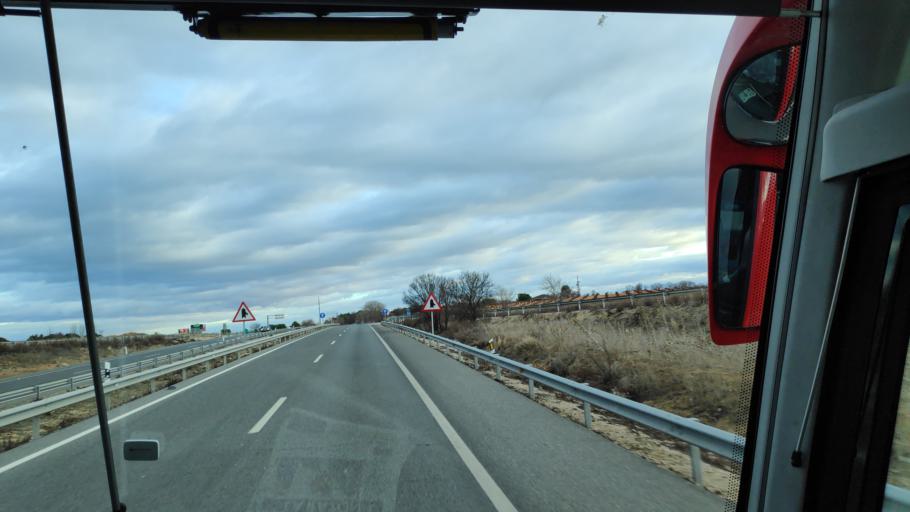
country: ES
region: Madrid
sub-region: Provincia de Madrid
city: Villarejo de Salvanes
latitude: 40.1712
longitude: -3.2919
